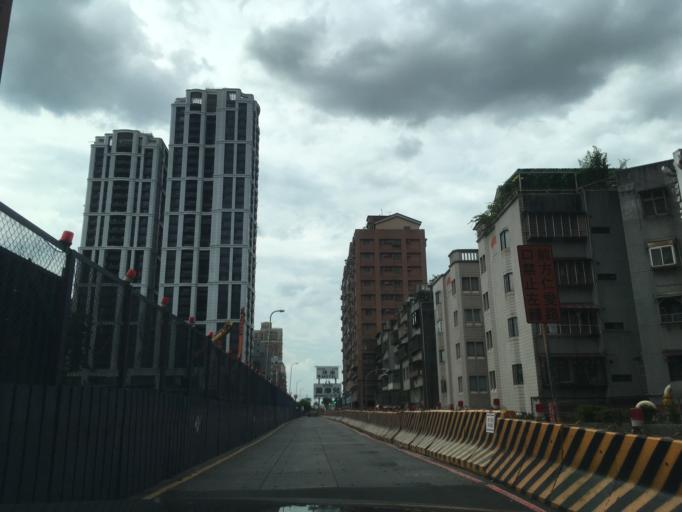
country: TW
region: Taipei
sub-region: Taipei
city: Banqiao
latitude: 25.0079
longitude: 121.5062
